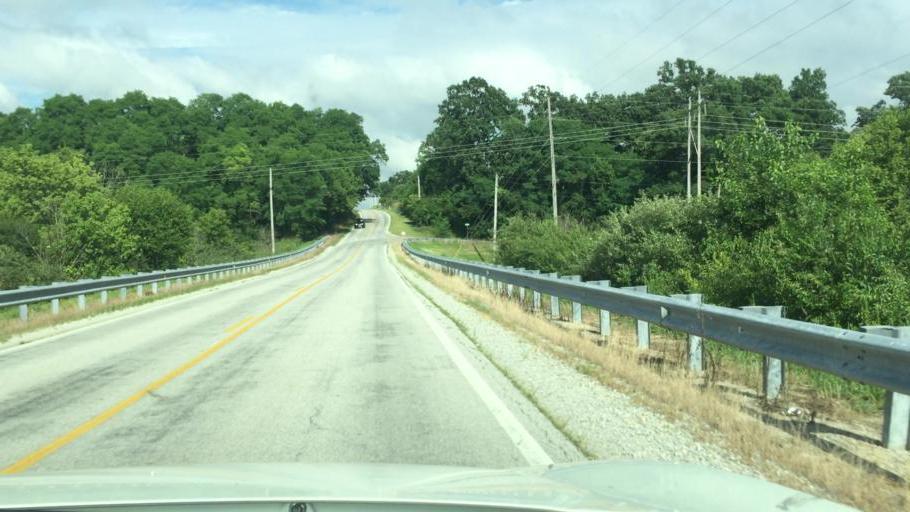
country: US
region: Ohio
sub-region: Clark County
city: Northridge
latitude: 39.9915
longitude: -83.7061
